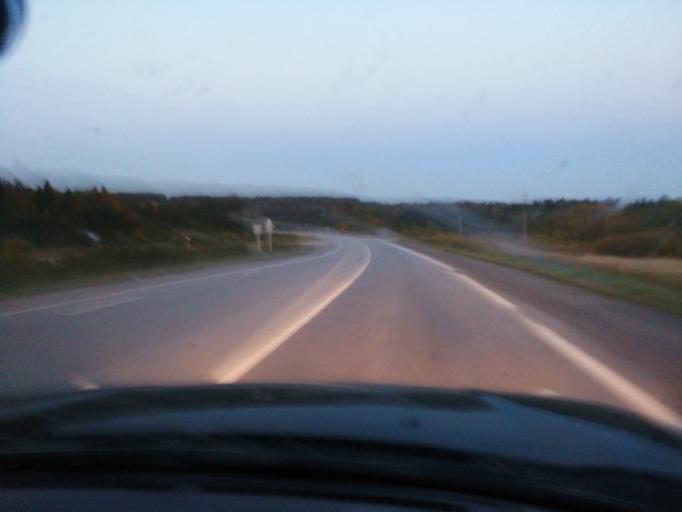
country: RU
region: Perm
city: Verkhnechusovskiye Gorodki
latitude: 58.2646
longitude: 57.3339
